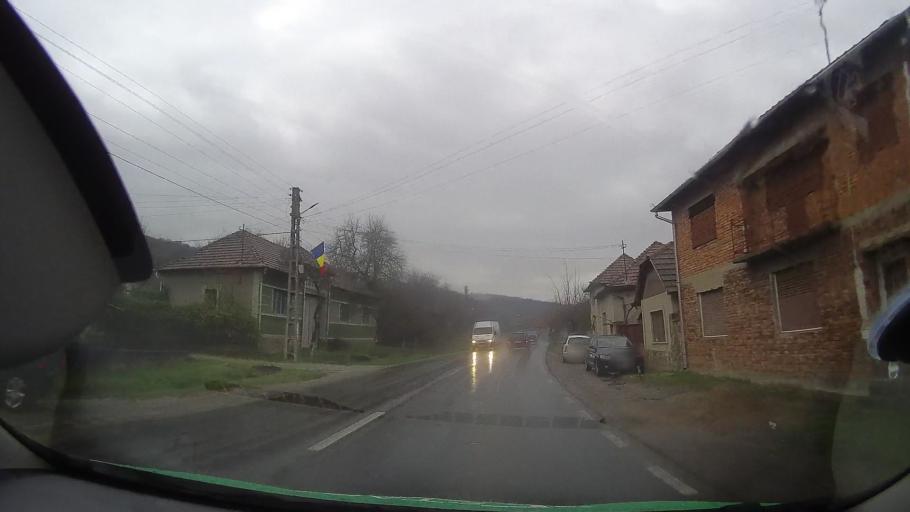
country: RO
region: Bihor
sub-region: Comuna Rabagani
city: Rabagani
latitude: 46.7588
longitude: 22.1982
